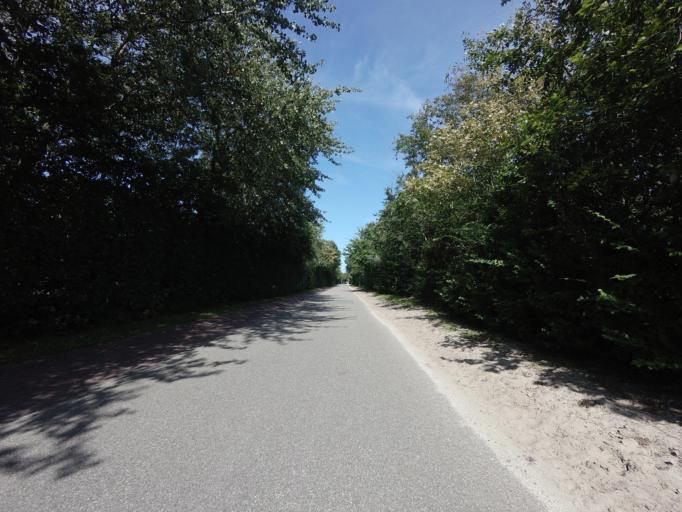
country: NL
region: Friesland
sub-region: Gemeente Ameland
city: Hollum
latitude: 53.4475
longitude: 5.6360
